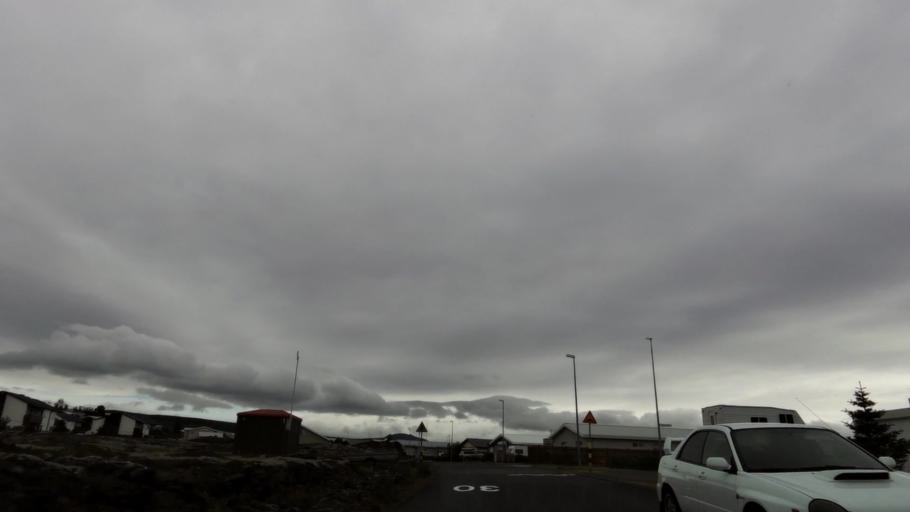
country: IS
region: Capital Region
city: Alftanes
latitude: 64.0553
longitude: -21.9921
